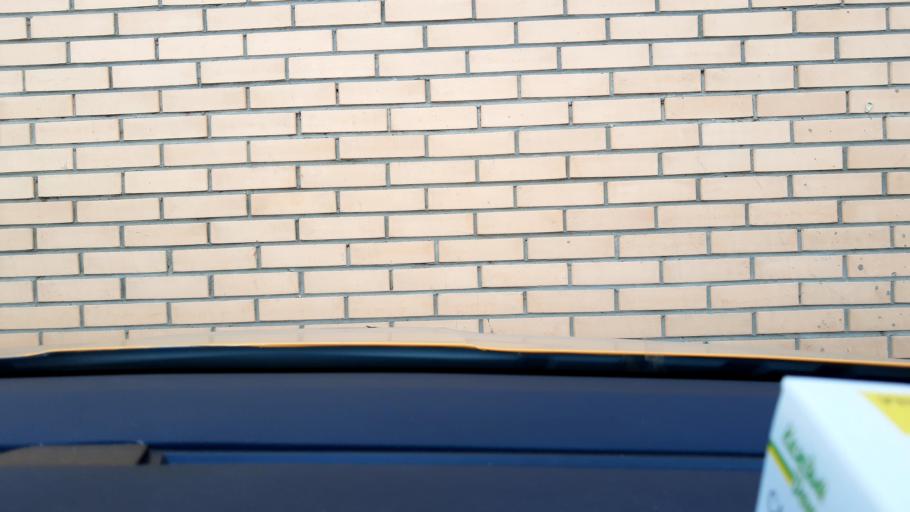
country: RU
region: Moscow
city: Kuz'minki
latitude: 55.6780
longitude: 37.7996
